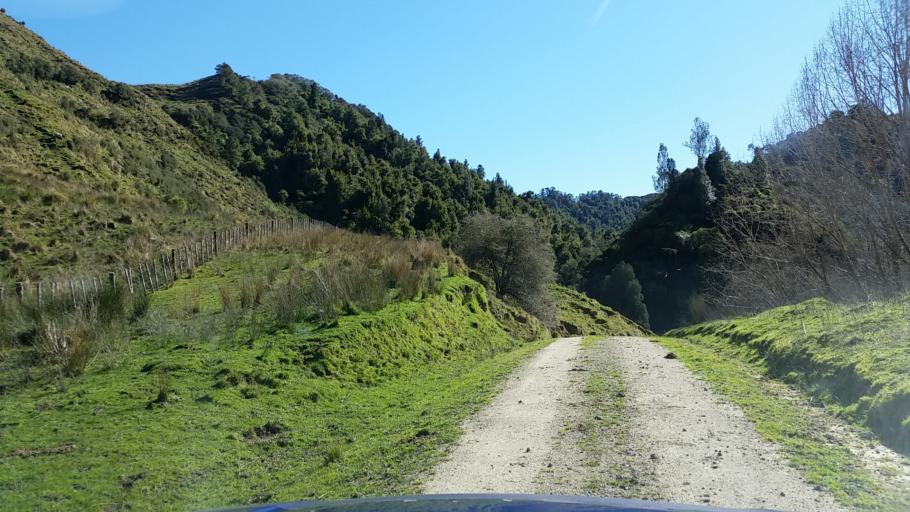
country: NZ
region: Manawatu-Wanganui
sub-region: Wanganui District
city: Wanganui
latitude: -39.6693
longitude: 174.8572
